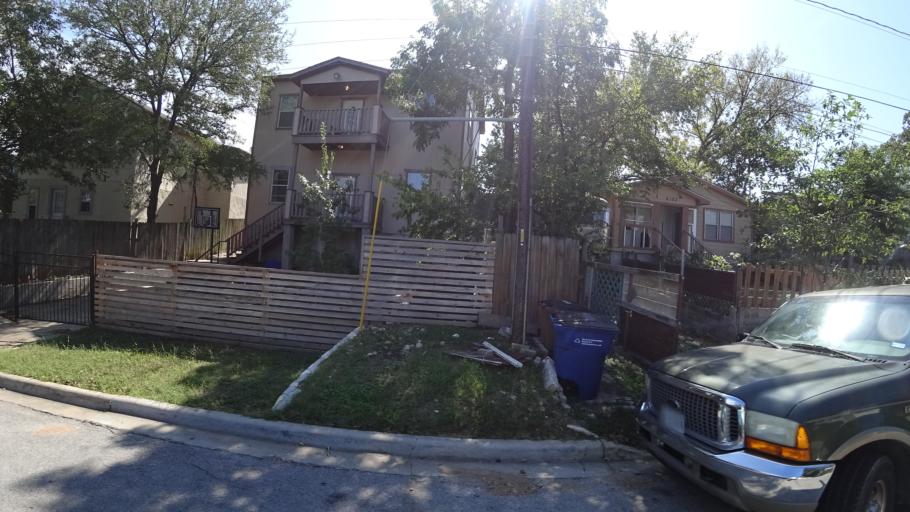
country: US
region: Texas
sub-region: Travis County
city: Austin
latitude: 30.2644
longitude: -97.7183
